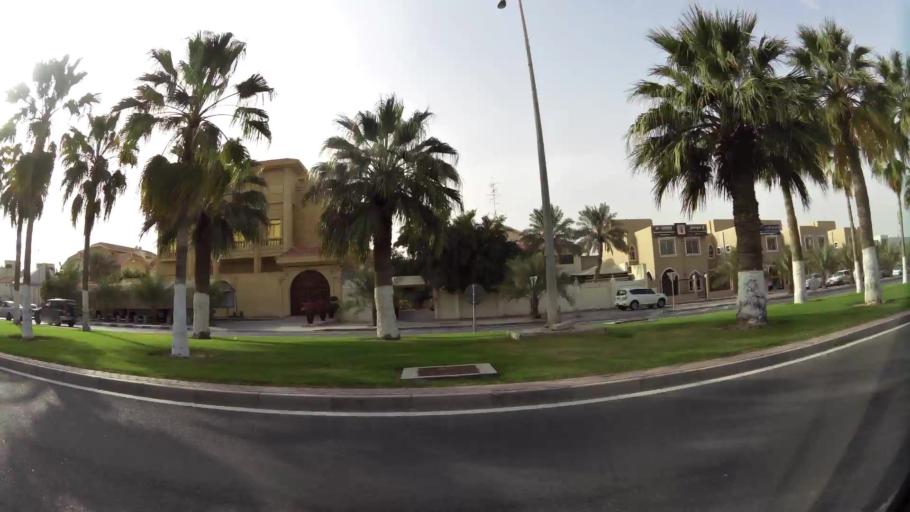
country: QA
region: Baladiyat ad Dawhah
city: Doha
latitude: 25.3225
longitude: 51.4996
